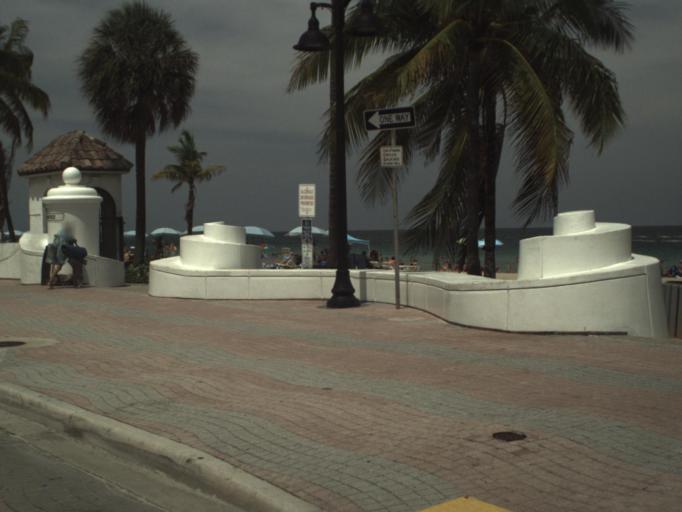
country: US
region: Florida
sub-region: Broward County
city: Sunrise
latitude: 26.1217
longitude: -80.1042
